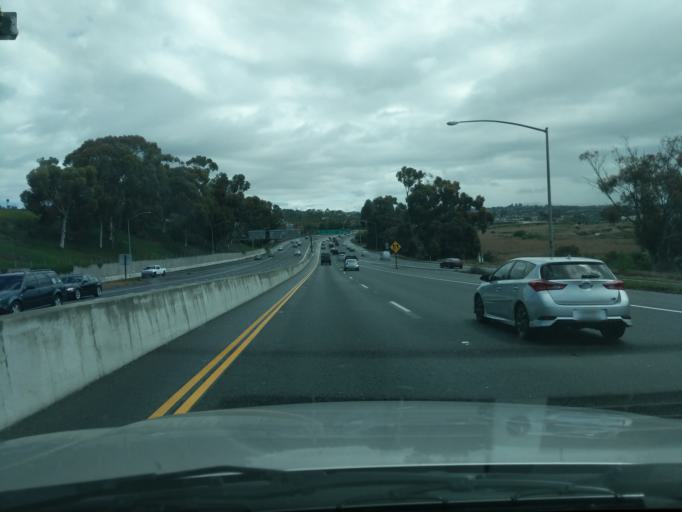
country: US
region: California
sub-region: San Diego County
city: Carlsbad
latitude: 33.1779
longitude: -117.3497
